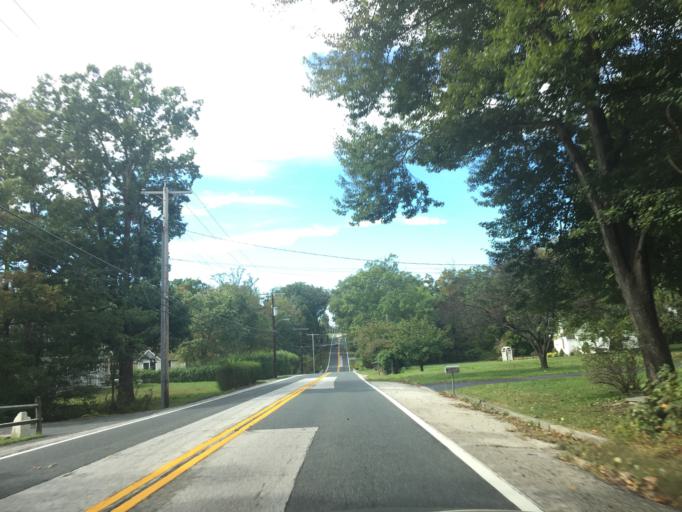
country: US
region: Maryland
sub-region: Baltimore County
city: Kingsville
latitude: 39.4212
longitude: -76.3875
